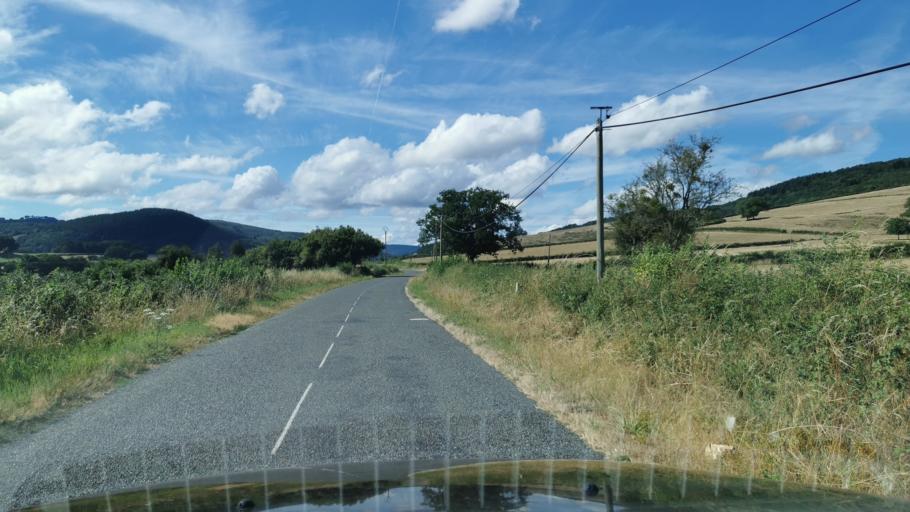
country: FR
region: Bourgogne
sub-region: Departement de Saone-et-Loire
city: Marmagne
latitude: 46.8164
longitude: 4.3283
